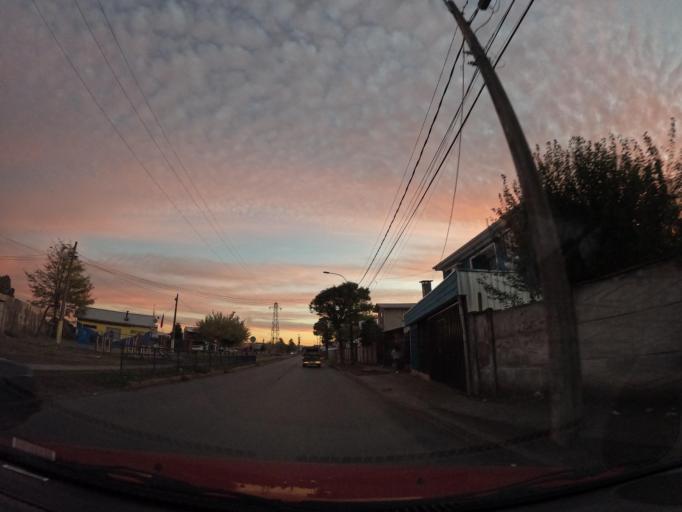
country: CL
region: Biobio
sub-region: Provincia de Nuble
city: Chillan
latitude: -36.6290
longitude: -72.0957
